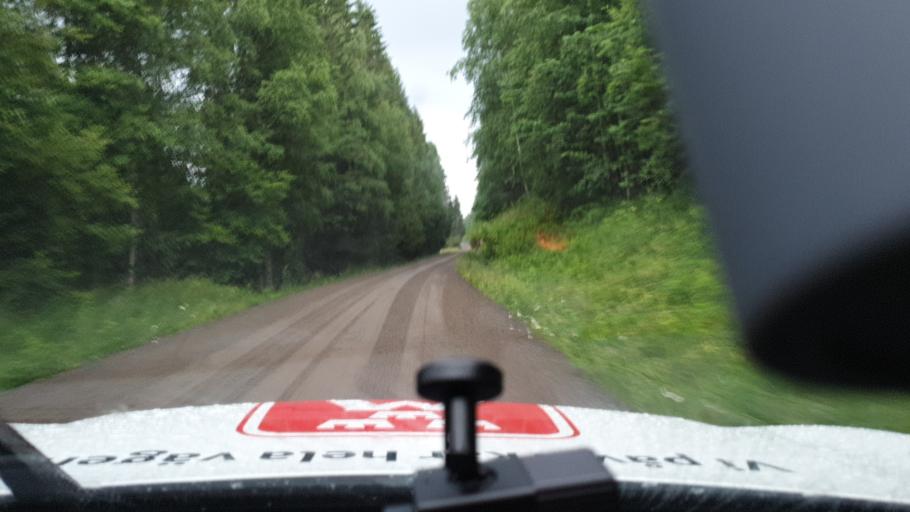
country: SE
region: Vaermland
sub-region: Hagfors Kommun
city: Ekshaerad
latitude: 60.4301
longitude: 13.2361
